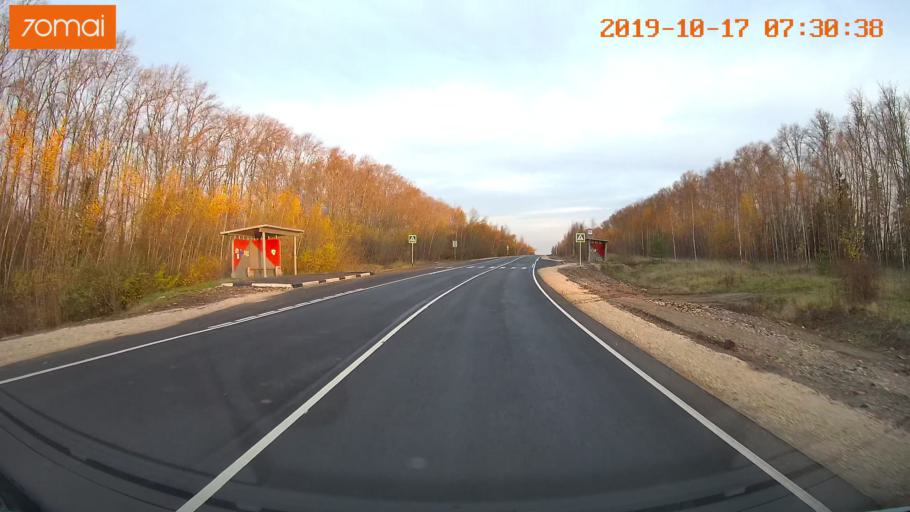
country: RU
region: Ivanovo
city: Gavrilov Posad
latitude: 56.3793
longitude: 40.0074
